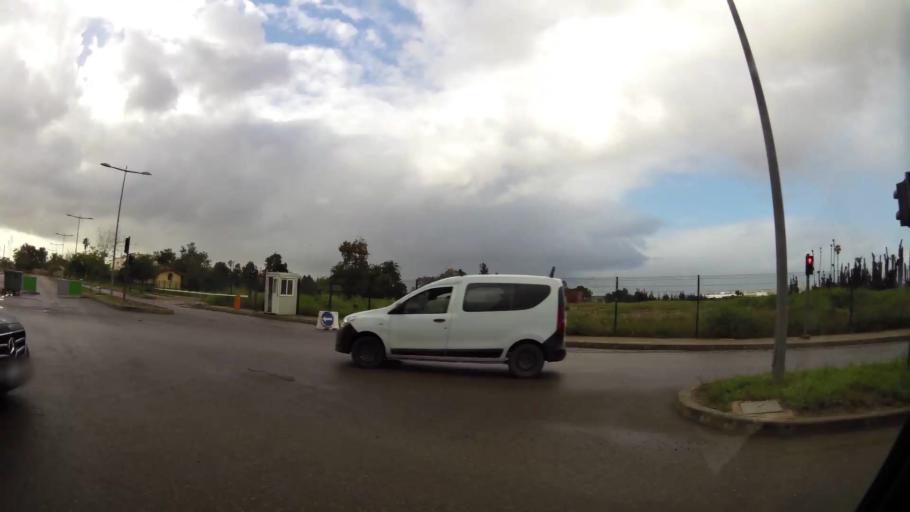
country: MA
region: Grand Casablanca
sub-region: Casablanca
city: Casablanca
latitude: 33.5593
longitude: -7.6570
